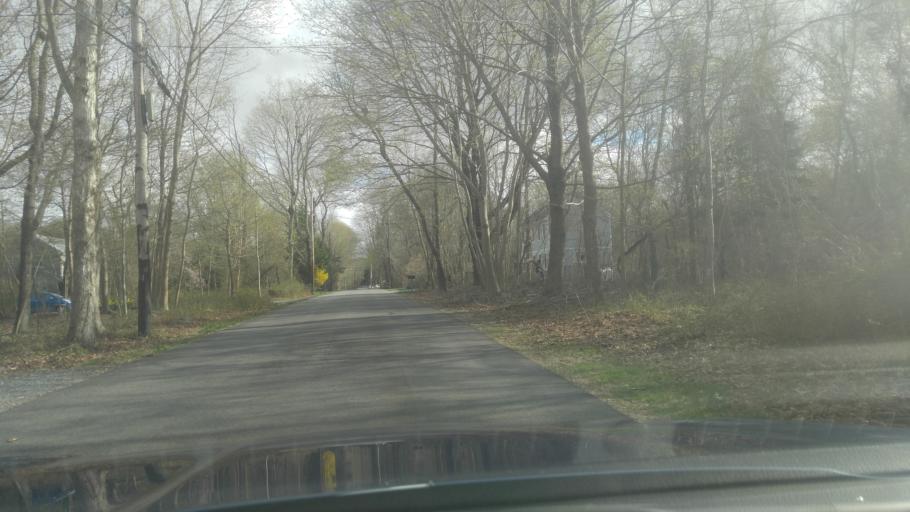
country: US
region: Rhode Island
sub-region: Newport County
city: Jamestown
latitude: 41.5665
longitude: -71.3727
